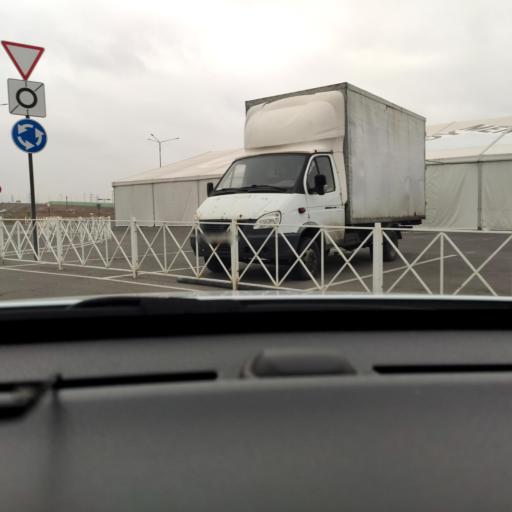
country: RU
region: Voronezj
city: Novaya Usman'
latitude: 51.6496
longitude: 39.3114
